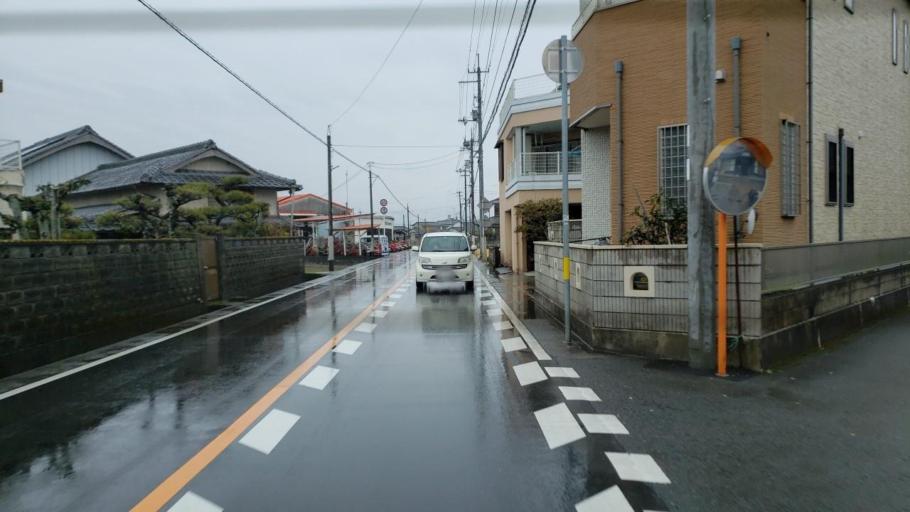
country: JP
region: Tokushima
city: Kamojimacho-jogejima
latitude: 34.0992
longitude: 134.3758
